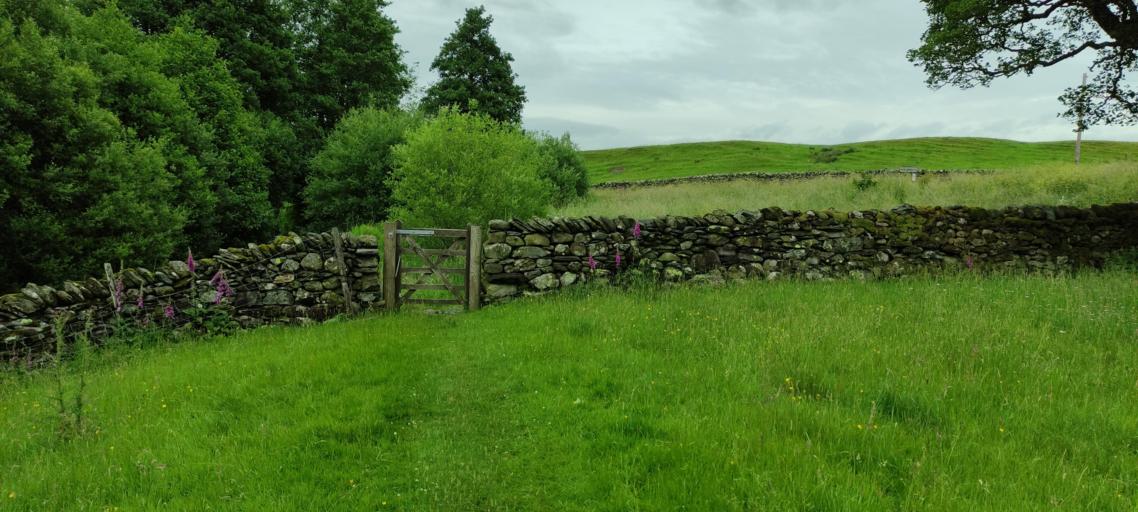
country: GB
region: England
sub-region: Cumbria
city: Keswick
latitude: 54.6599
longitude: -2.9853
